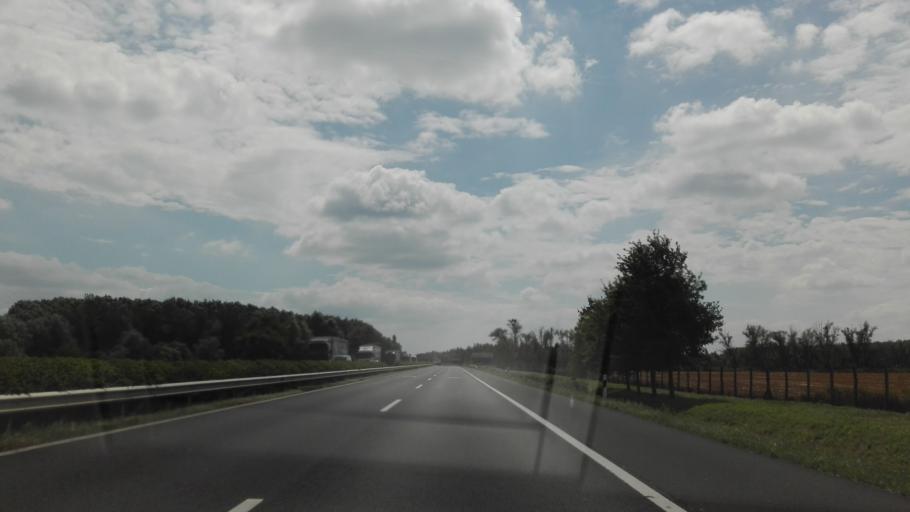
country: HU
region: Gyor-Moson-Sopron
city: Mosonmagyarovar
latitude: 47.8143
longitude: 17.2920
